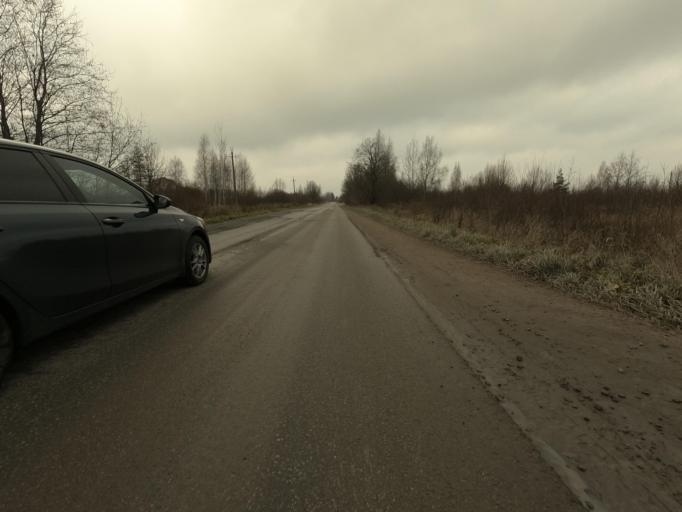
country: RU
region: Leningrad
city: Lyuban'
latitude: 59.4816
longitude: 31.2622
